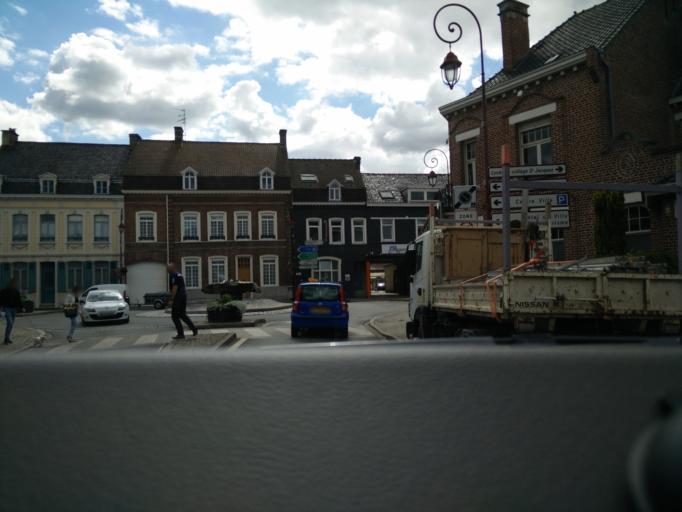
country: FR
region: Nord-Pas-de-Calais
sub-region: Departement du Nord
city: Hazebrouck
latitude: 50.7244
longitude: 2.5339
